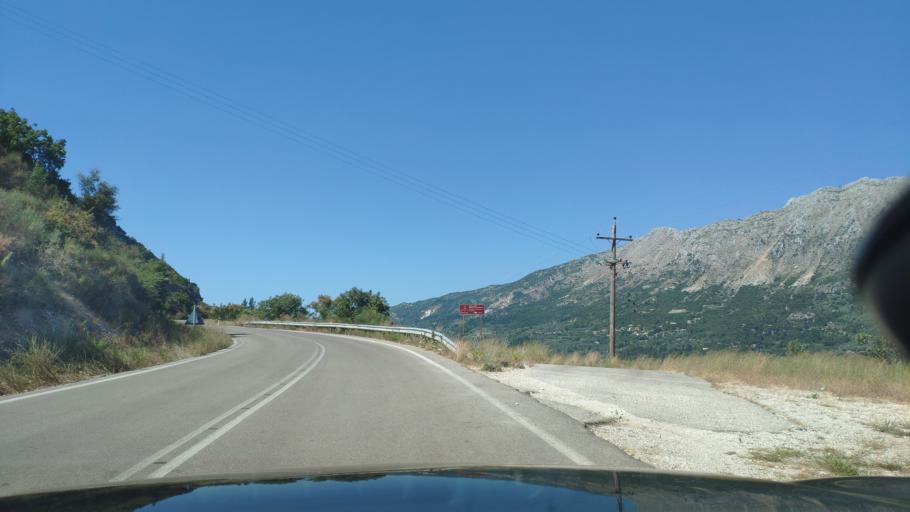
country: GR
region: Ionian Islands
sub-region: Lefkada
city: Nidri
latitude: 38.6783
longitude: 20.5969
